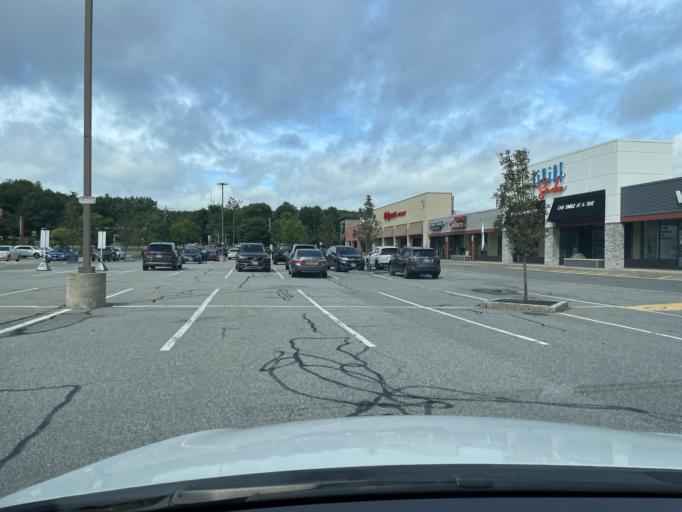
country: US
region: Massachusetts
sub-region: Middlesex County
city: Woburn
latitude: 42.4610
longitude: -71.1635
